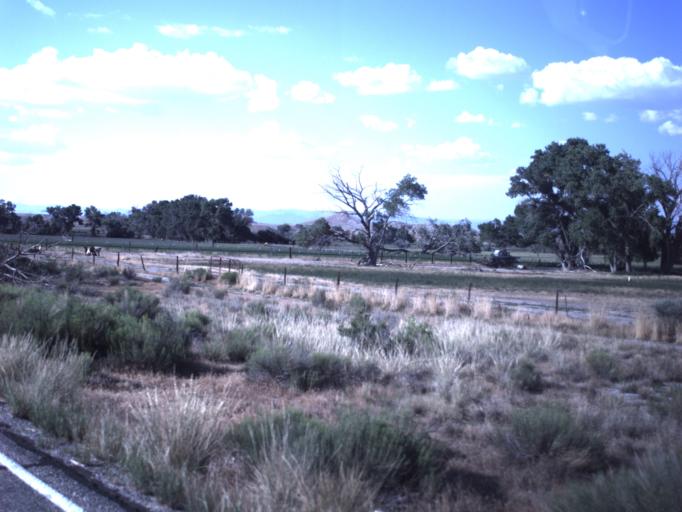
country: US
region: Utah
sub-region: Emery County
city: Huntington
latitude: 39.4209
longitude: -110.8586
